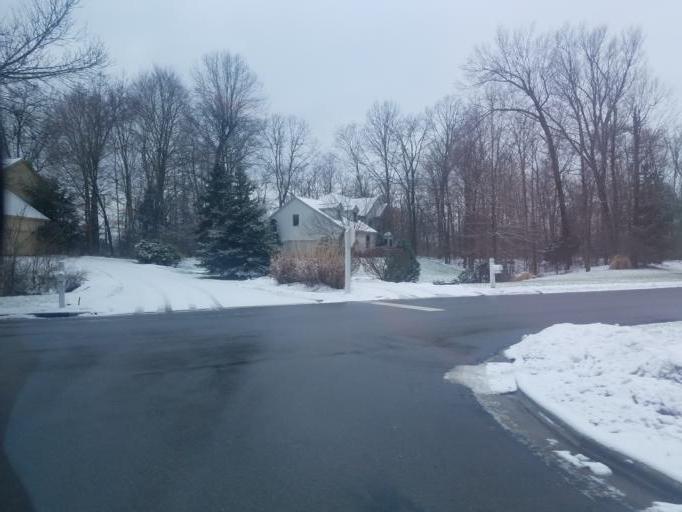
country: US
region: Ohio
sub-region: Franklin County
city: New Albany
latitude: 40.0483
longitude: -82.8296
